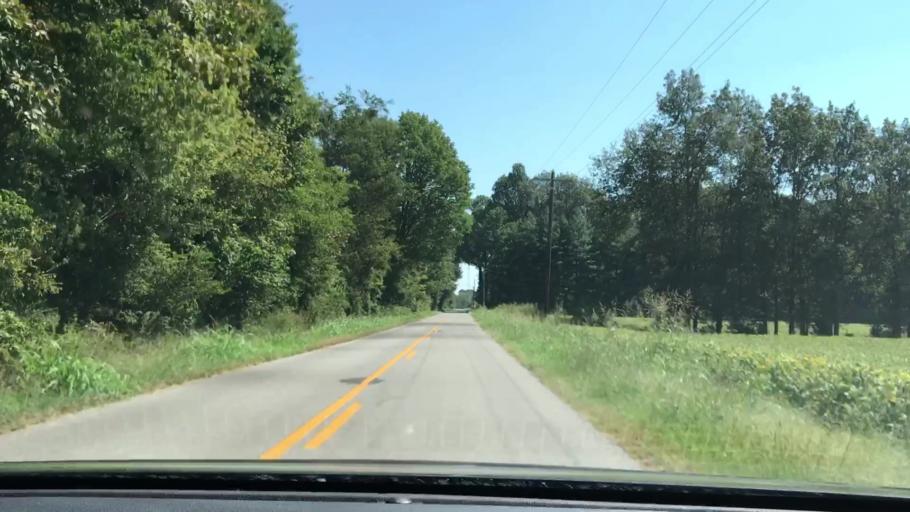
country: US
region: Kentucky
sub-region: Fulton County
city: Fulton
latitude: 36.5222
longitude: -88.8987
